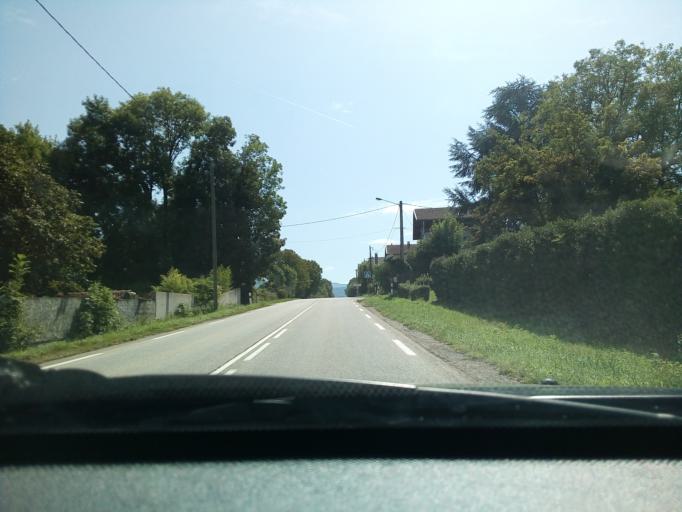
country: FR
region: Rhone-Alpes
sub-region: Departement de l'Isere
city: Brie-et-Angonnes
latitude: 45.1299
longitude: 5.7772
